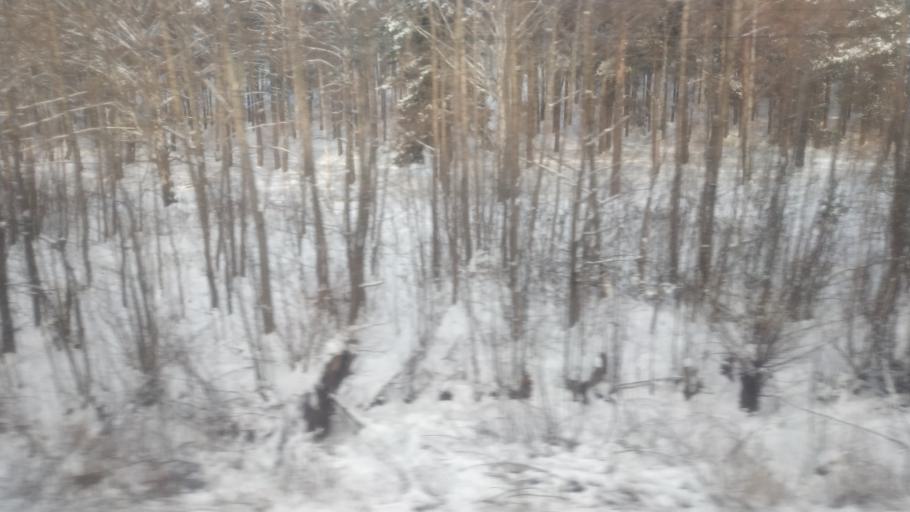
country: RU
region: Kirov
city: Krasnaya Polyana
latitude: 56.2497
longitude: 51.1524
